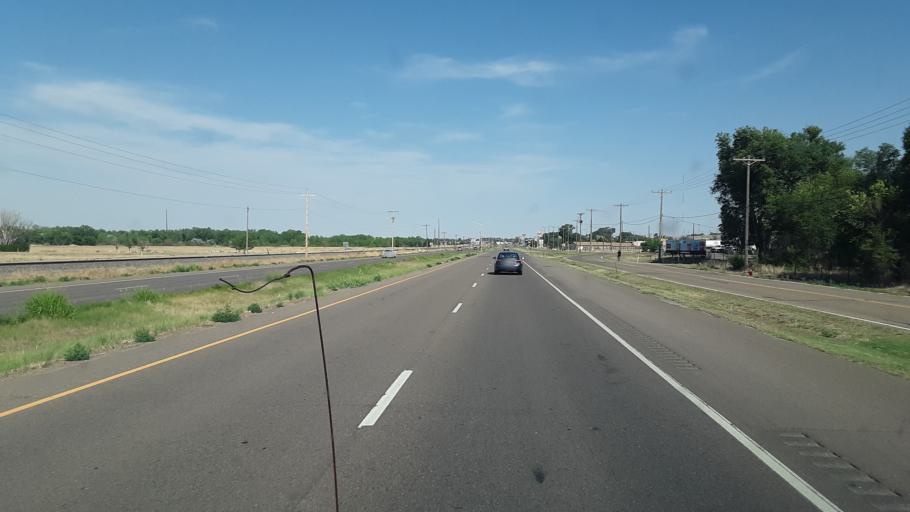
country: US
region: Colorado
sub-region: Otero County
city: La Junta
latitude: 37.9958
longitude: -103.5803
